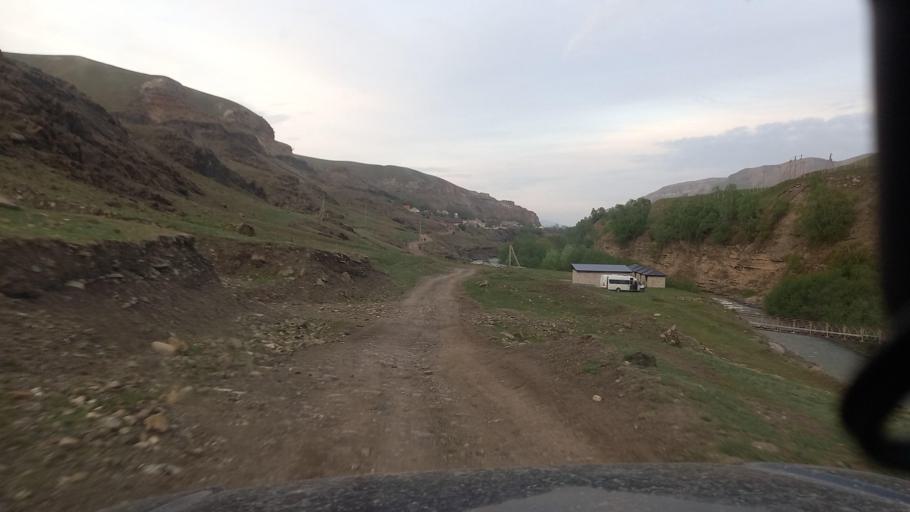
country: RU
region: Kabardino-Balkariya
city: Kamennomostskoye
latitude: 43.7238
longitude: 42.9049
